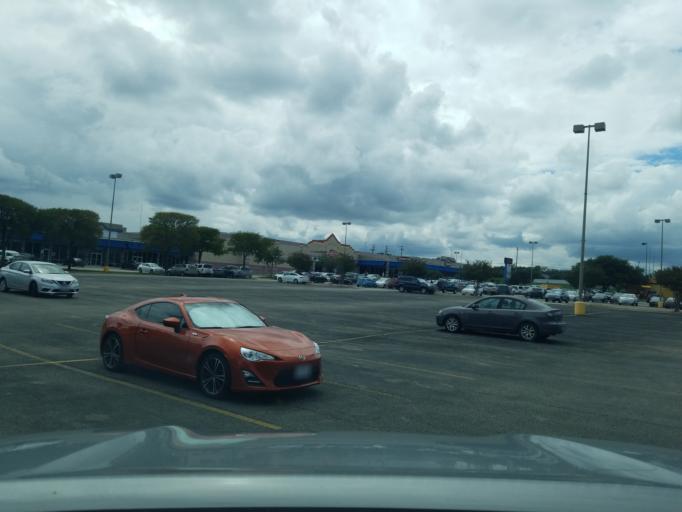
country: US
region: Texas
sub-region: Williamson County
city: Anderson Mill
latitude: 30.4599
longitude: -97.7907
